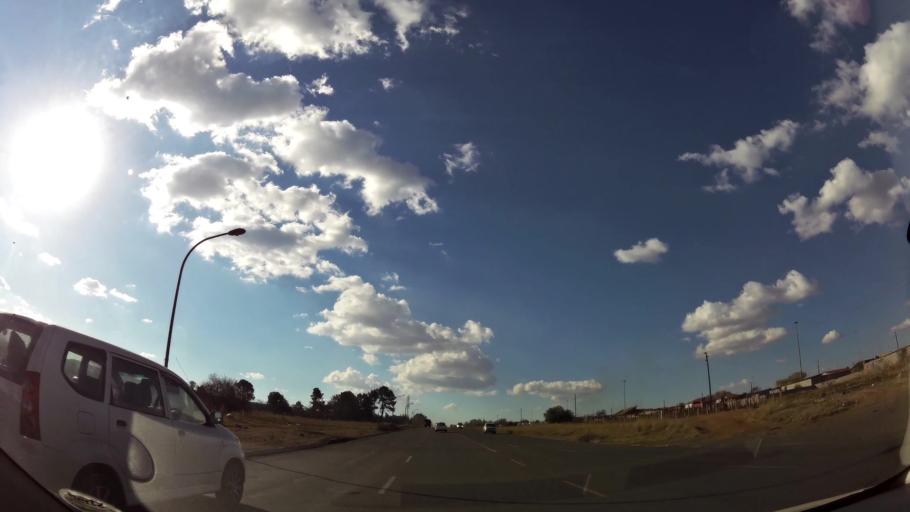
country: ZA
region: Mpumalanga
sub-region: Nkangala District Municipality
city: Witbank
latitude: -25.8751
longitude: 29.1652
